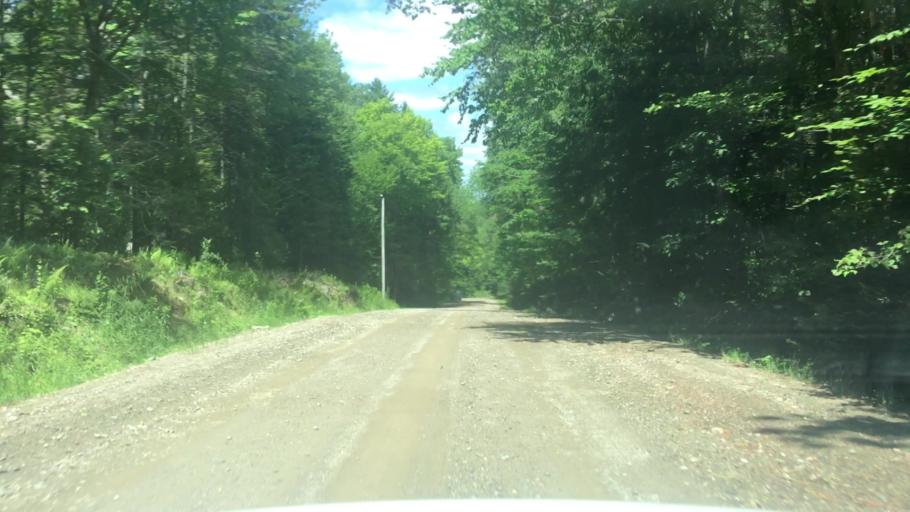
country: US
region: Maine
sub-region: Waldo County
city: Searsmont
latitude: 44.4729
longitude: -69.2973
